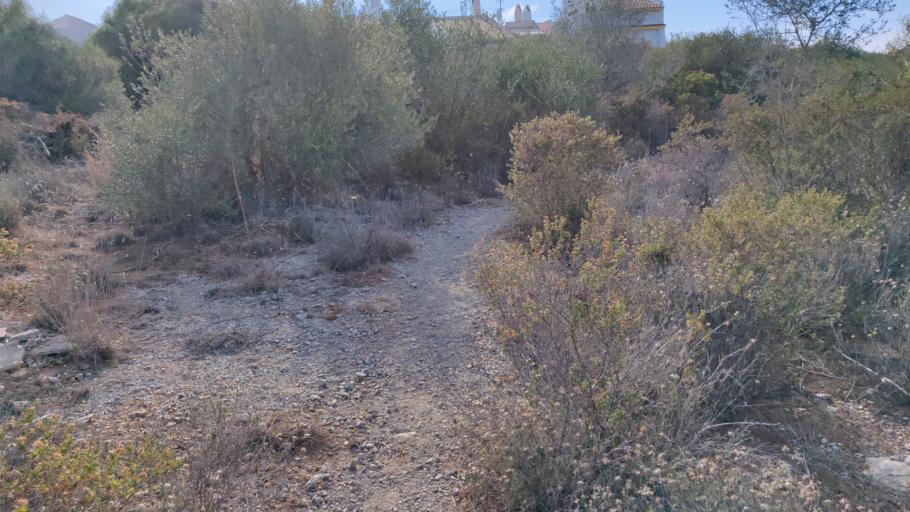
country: ES
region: Balearic Islands
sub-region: Illes Balears
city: Felanitx
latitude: 39.4525
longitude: 3.2626
